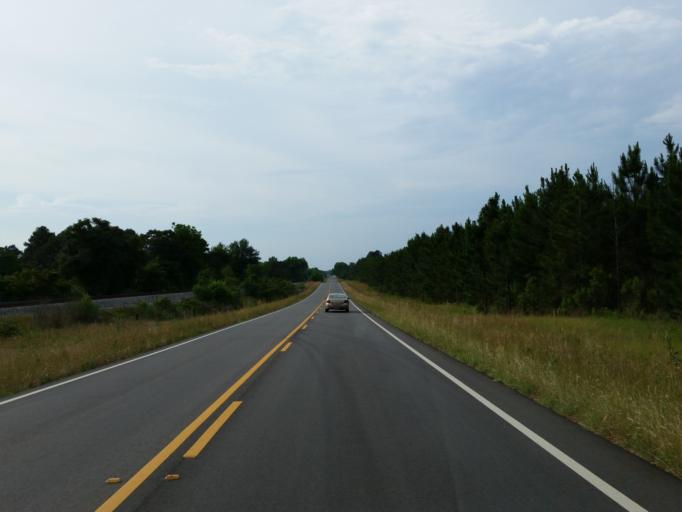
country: US
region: Georgia
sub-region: Turner County
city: Ashburn
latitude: 31.6249
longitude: -83.6094
